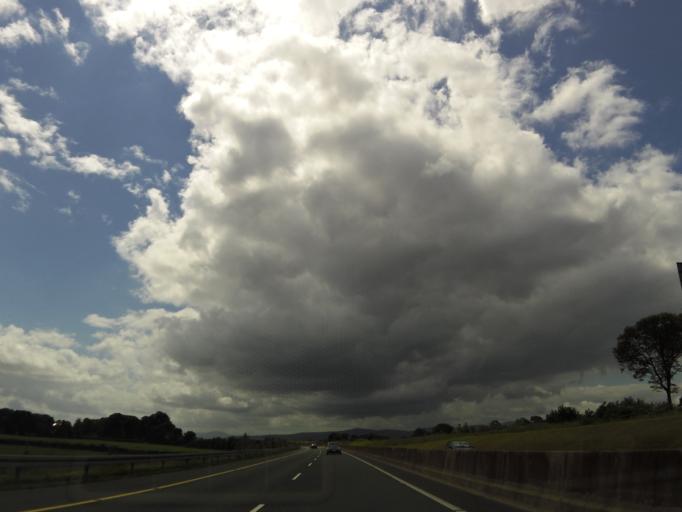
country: IE
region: Munster
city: Cashel
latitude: 52.4877
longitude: -7.9018
